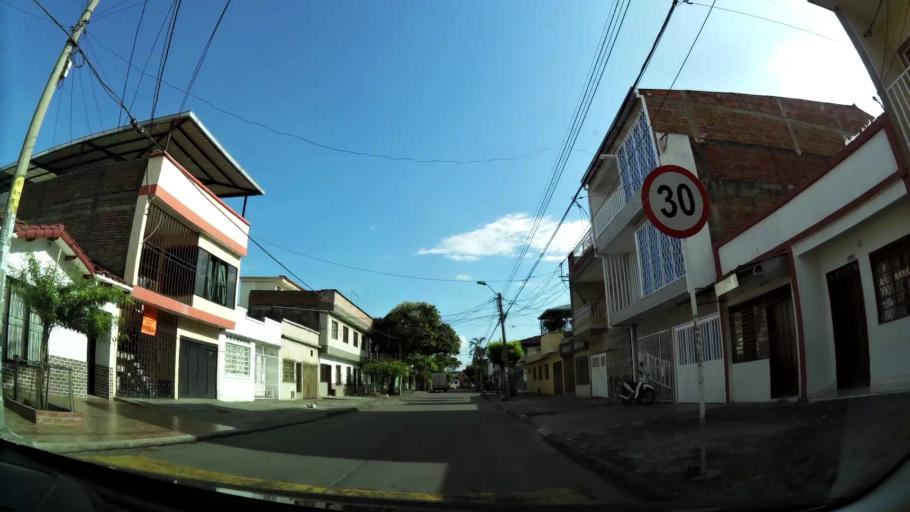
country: CO
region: Valle del Cauca
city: Cali
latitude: 3.4273
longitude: -76.5251
